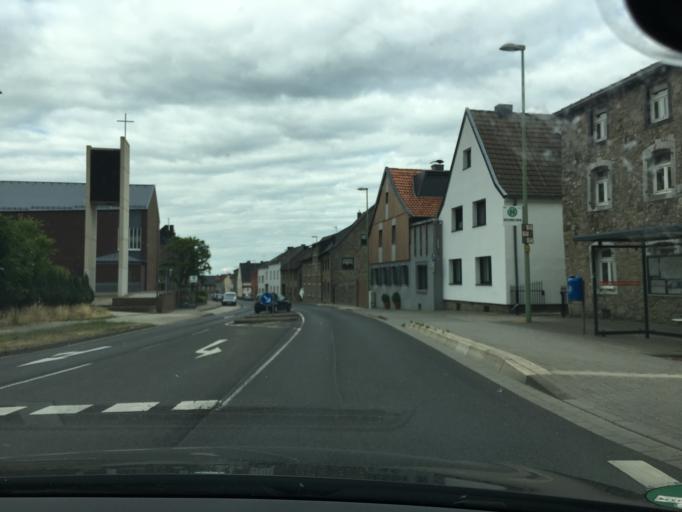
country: DE
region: North Rhine-Westphalia
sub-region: Regierungsbezirk Koln
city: Eschweiler
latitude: 50.7723
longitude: 6.2988
